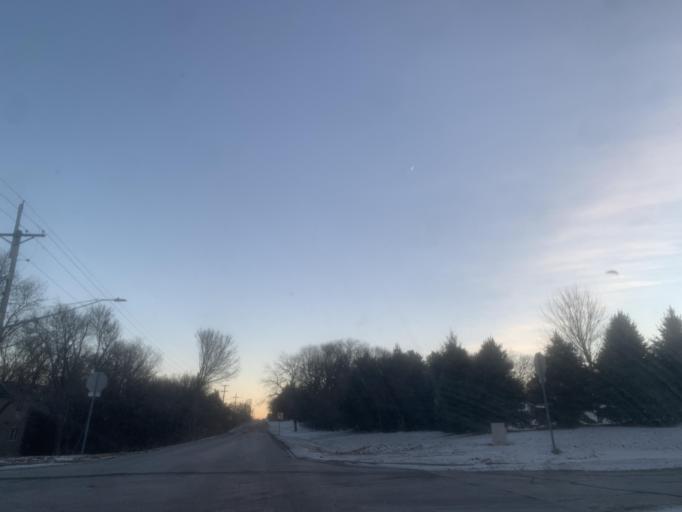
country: US
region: Nebraska
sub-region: Douglas County
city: Ralston
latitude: 41.2671
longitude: -96.0622
